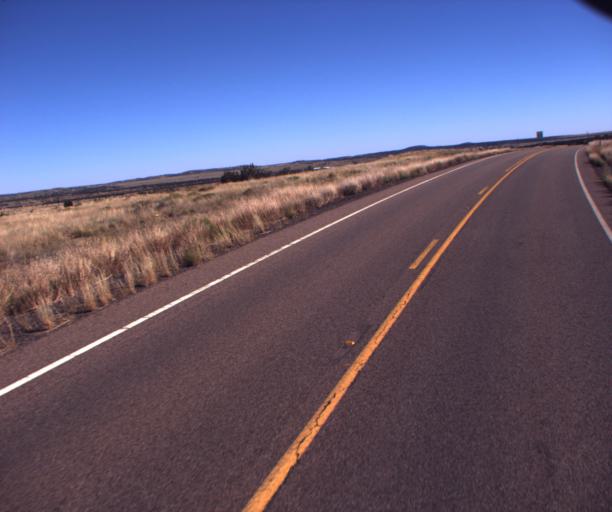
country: US
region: Arizona
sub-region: Navajo County
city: Taylor
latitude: 34.4826
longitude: -110.3333
